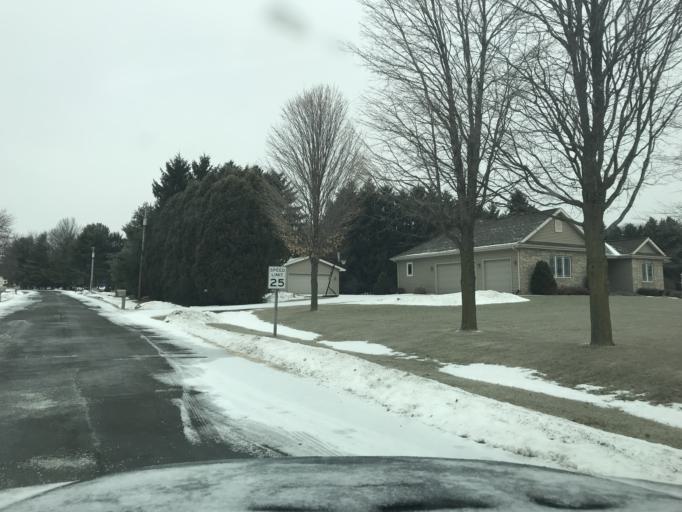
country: US
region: Wisconsin
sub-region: Dane County
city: Cottage Grove
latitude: 43.1043
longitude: -89.2317
